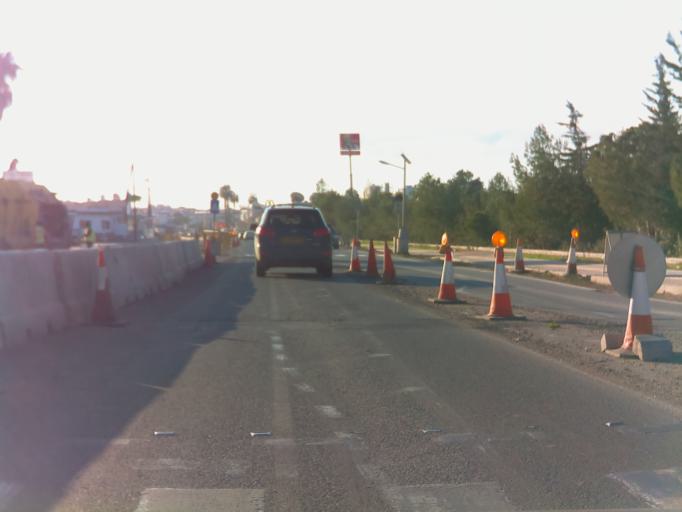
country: CY
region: Pafos
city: Paphos
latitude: 34.7752
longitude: 32.4085
